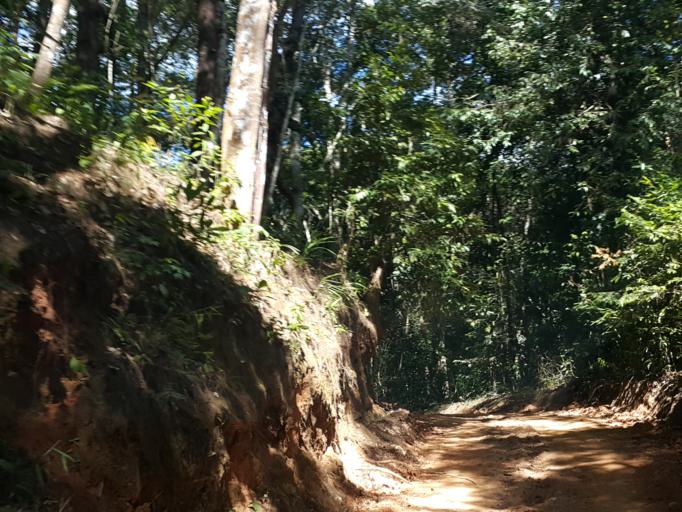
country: TH
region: Chiang Mai
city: Wiang Haeng
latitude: 19.5198
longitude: 98.8127
